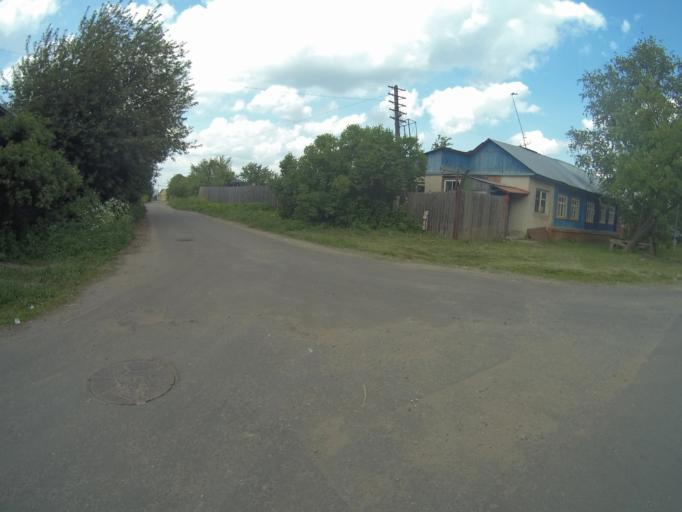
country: RU
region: Vladimir
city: Suzdal'
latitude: 56.4343
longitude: 40.4382
